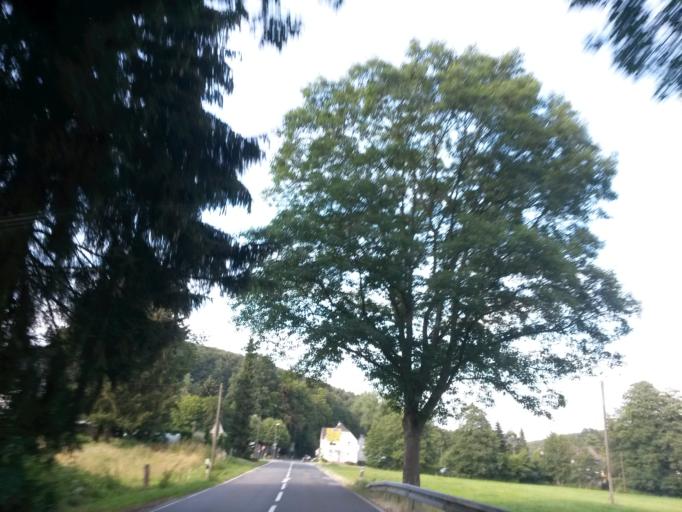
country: DE
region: North Rhine-Westphalia
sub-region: Regierungsbezirk Koln
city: Lindlar
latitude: 50.9889
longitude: 7.3192
